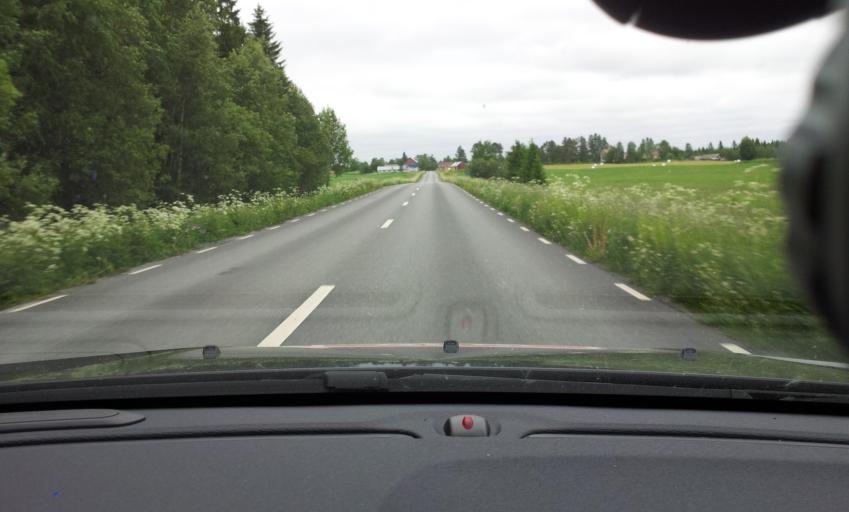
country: SE
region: Jaemtland
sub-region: Bergs Kommun
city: Hoverberg
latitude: 63.0585
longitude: 14.3277
